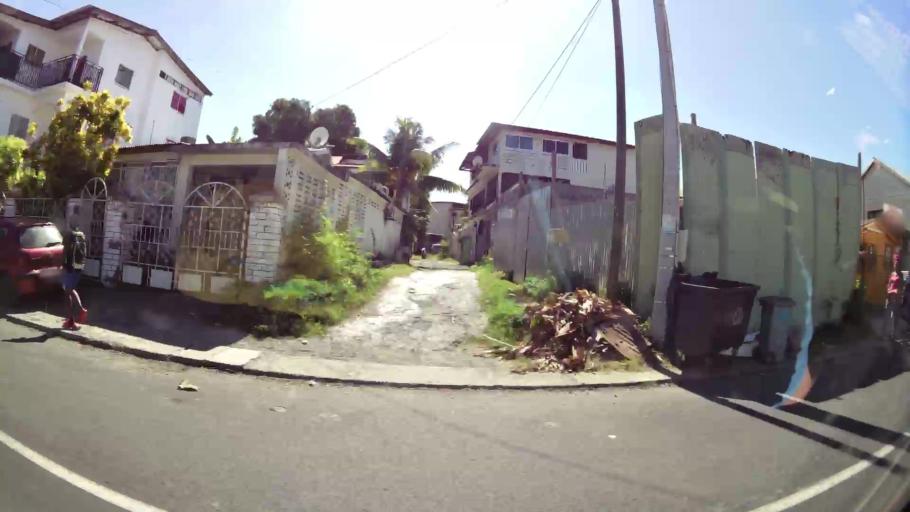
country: YT
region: Pamandzi
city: Pamandzi
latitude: -12.7851
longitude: 45.2777
